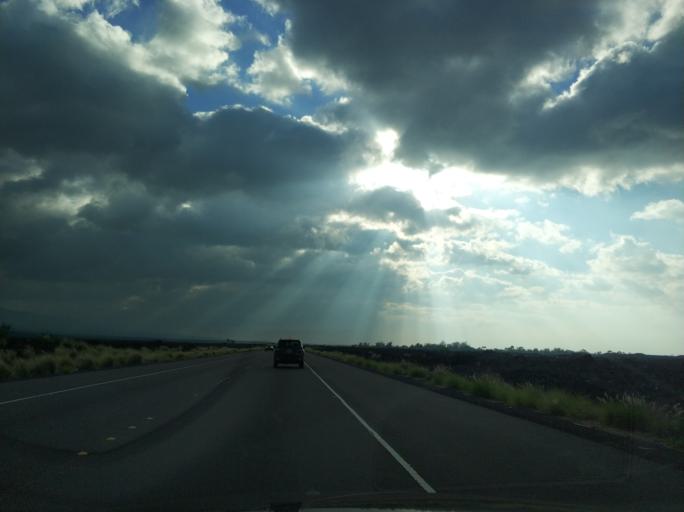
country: US
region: Hawaii
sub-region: Hawaii County
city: Waikoloa Village
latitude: 19.9289
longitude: -155.8512
